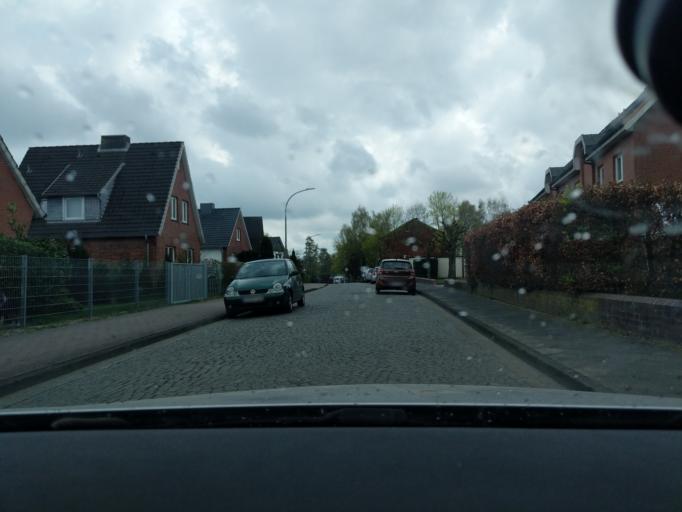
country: DE
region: Lower Saxony
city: Stade
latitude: 53.5838
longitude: 9.4931
